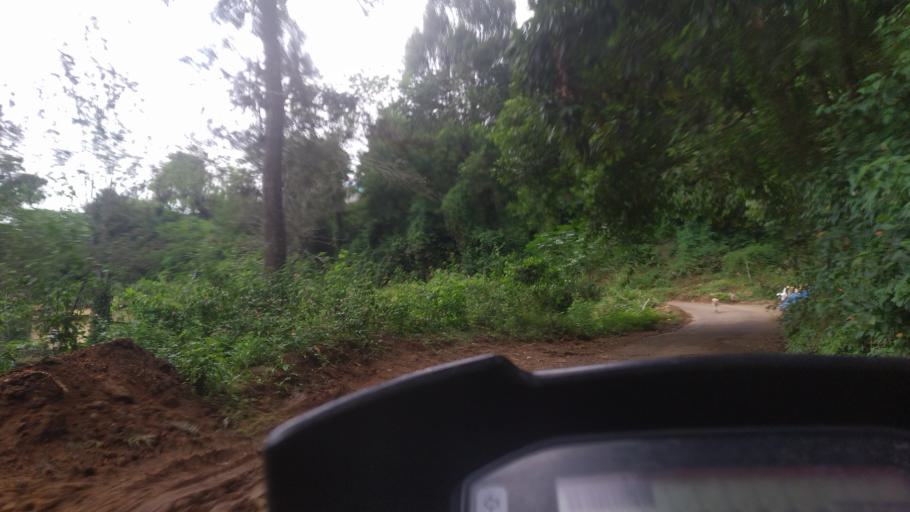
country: IN
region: Tamil Nadu
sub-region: Theni
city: Gudalur
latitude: 9.5754
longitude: 77.0825
